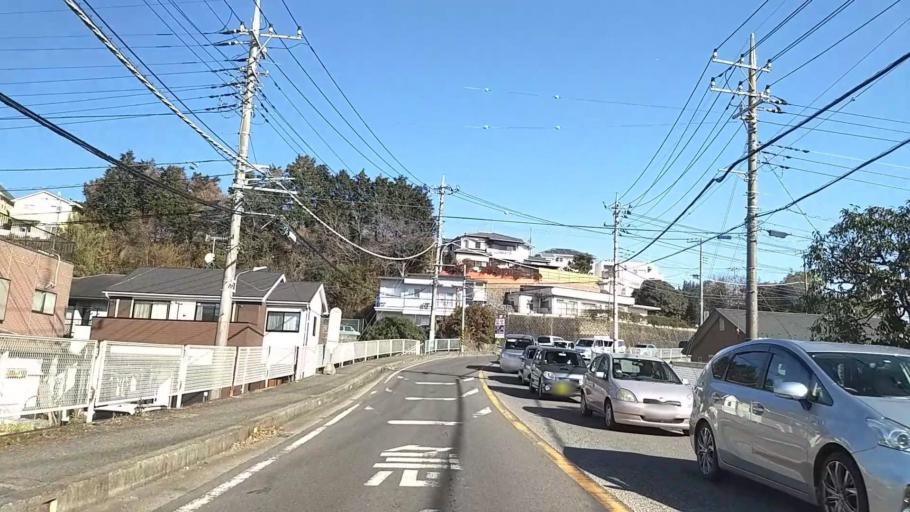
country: JP
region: Kanagawa
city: Hadano
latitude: 35.3782
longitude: 139.2090
